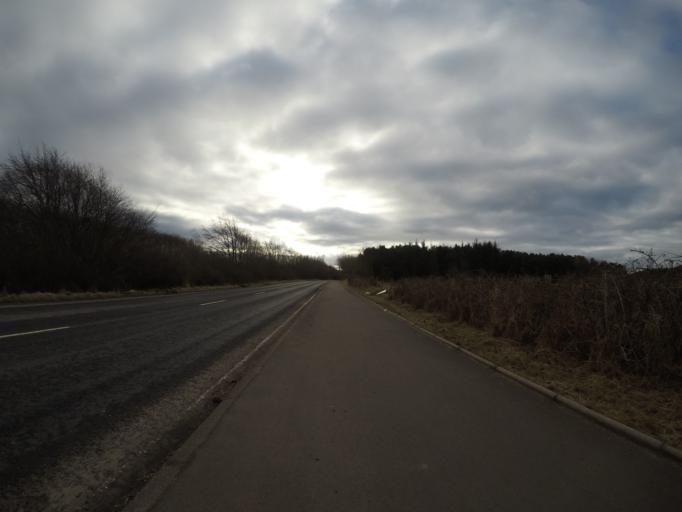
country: GB
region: Scotland
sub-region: North Ayrshire
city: Irvine
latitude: 55.5921
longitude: -4.6525
